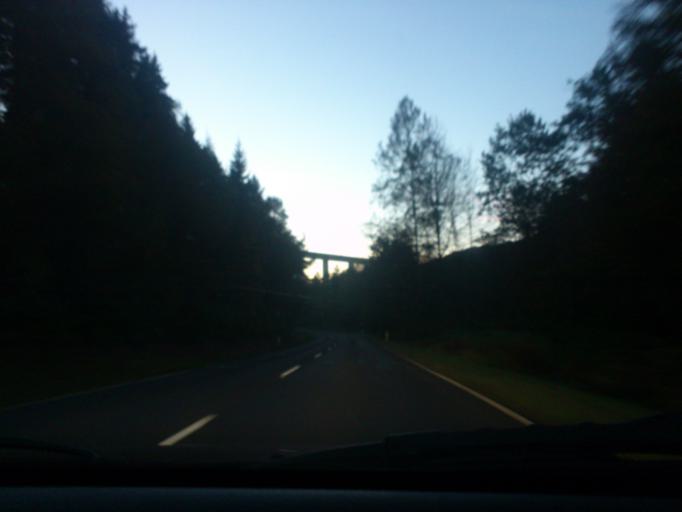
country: DE
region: Hesse
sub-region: Regierungsbezirk Giessen
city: Schlitz
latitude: 50.6721
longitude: 9.6337
